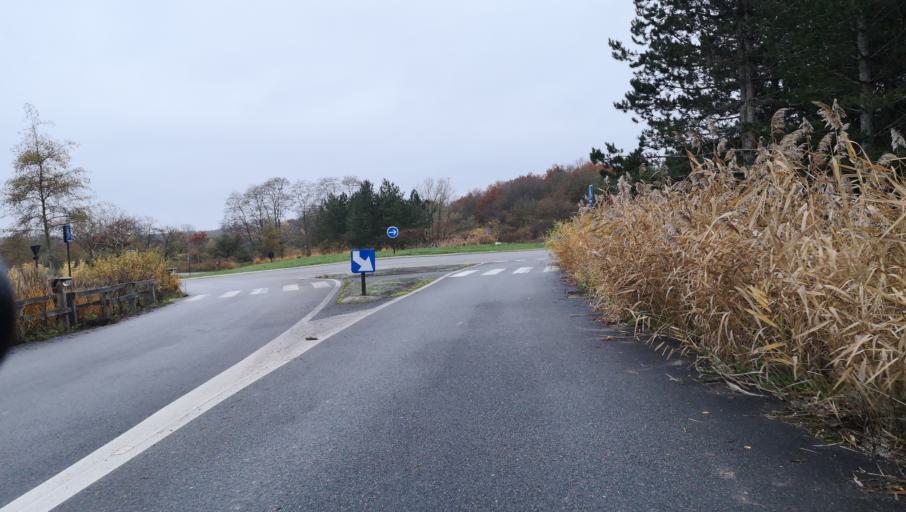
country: FR
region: Centre
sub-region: Departement du Loiret
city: Marigny-les-Usages
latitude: 47.9493
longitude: 2.0099
